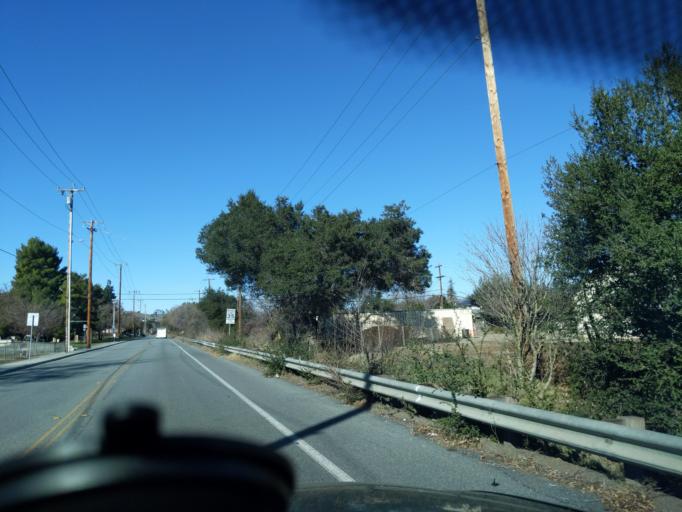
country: US
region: California
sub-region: Santa Clara County
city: Morgan Hill
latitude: 37.1299
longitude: -121.6598
